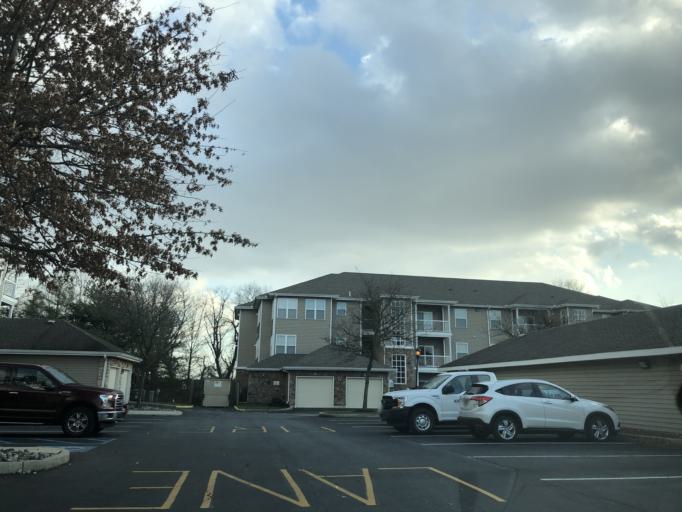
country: US
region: Delaware
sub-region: New Castle County
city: Bear
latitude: 39.6350
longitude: -75.6493
